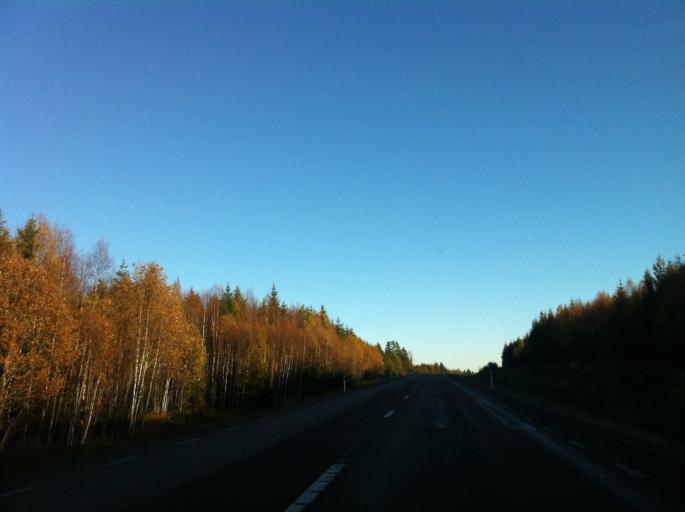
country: SE
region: Dalarna
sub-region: Rattviks Kommun
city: Raettvik
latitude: 60.8400
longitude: 15.2092
